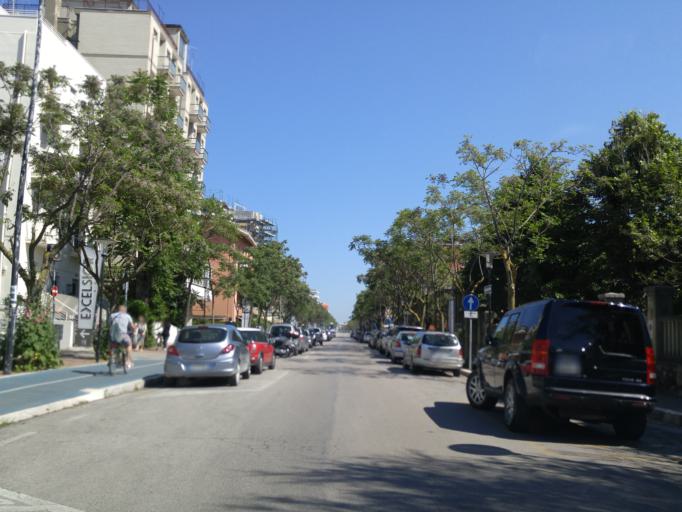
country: IT
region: The Marches
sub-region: Provincia di Pesaro e Urbino
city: Pesaro
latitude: 43.9112
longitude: 12.9215
